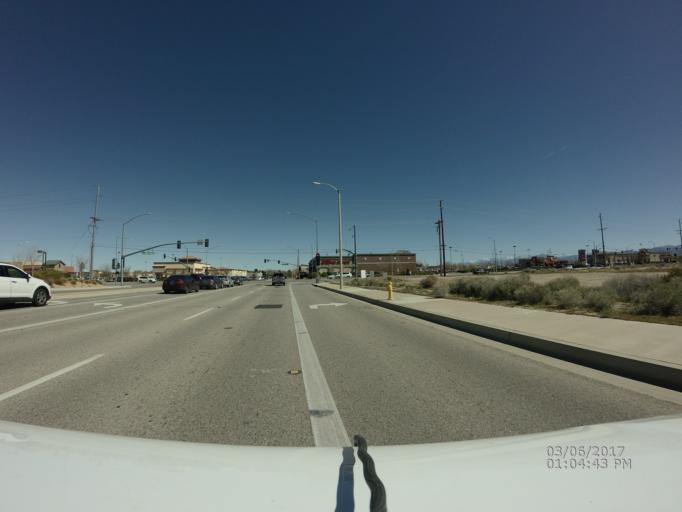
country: US
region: California
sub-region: Los Angeles County
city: Desert View Highlands
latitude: 34.6091
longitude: -118.1484
